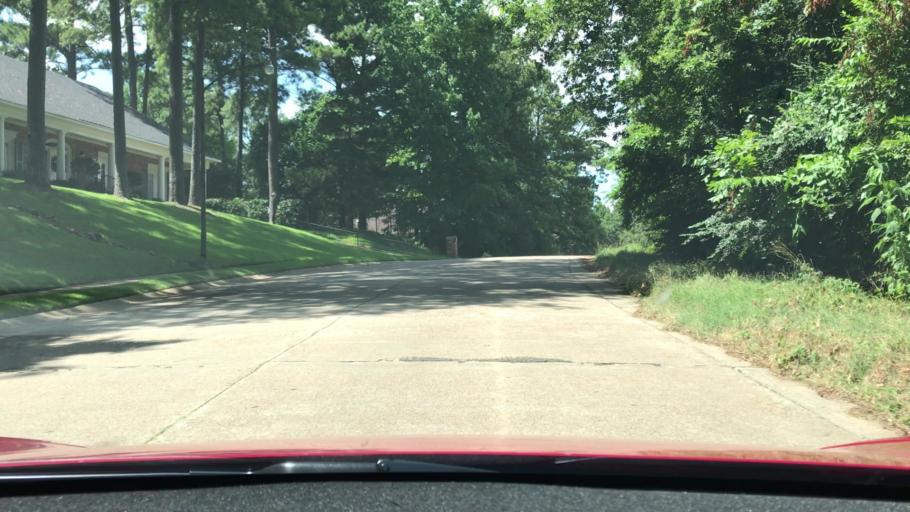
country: US
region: Louisiana
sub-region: Bossier Parish
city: Bossier City
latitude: 32.4226
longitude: -93.7287
